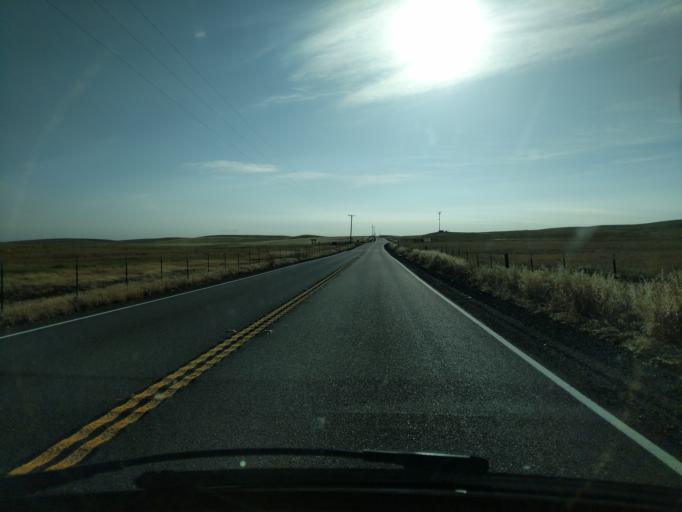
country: US
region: California
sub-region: Stanislaus County
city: East Oakdale
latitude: 37.9448
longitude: -120.8326
